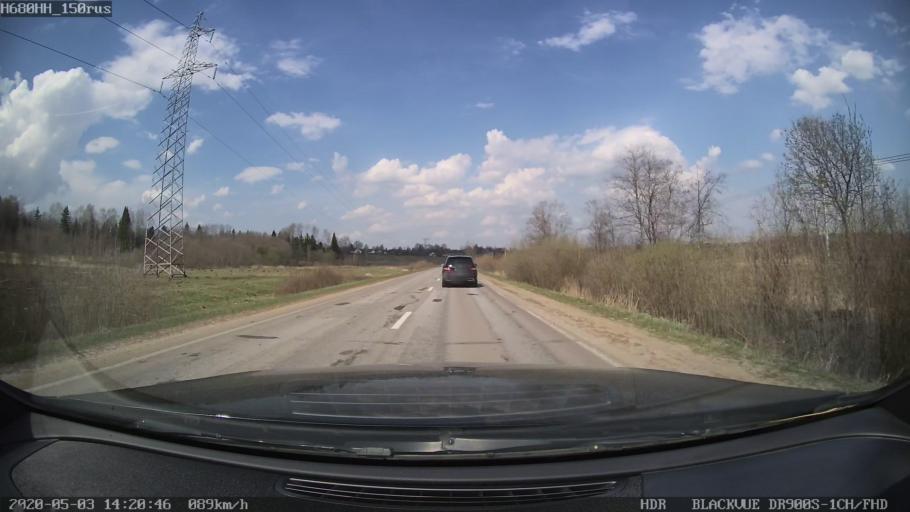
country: RU
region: Moskovskaya
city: Solnechnogorsk
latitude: 56.2481
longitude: 36.9719
